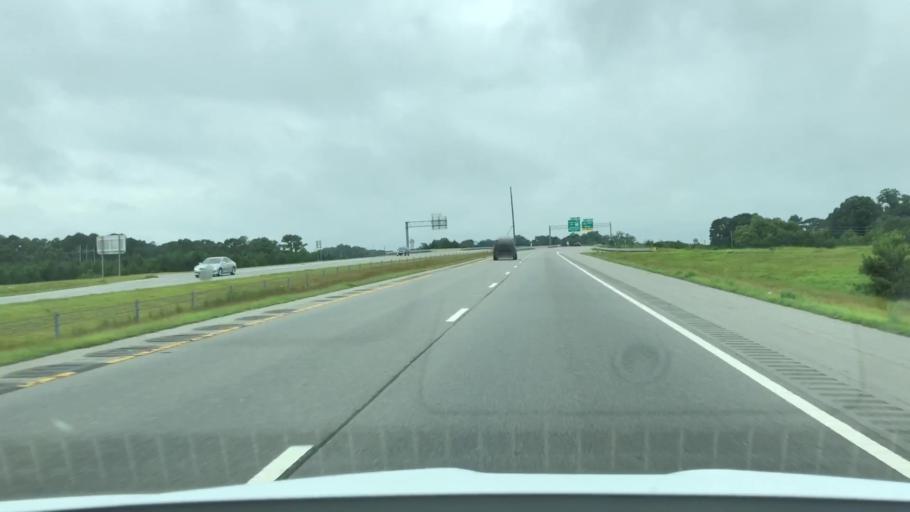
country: US
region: North Carolina
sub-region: Wayne County
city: Goldsboro
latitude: 35.4258
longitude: -77.9777
